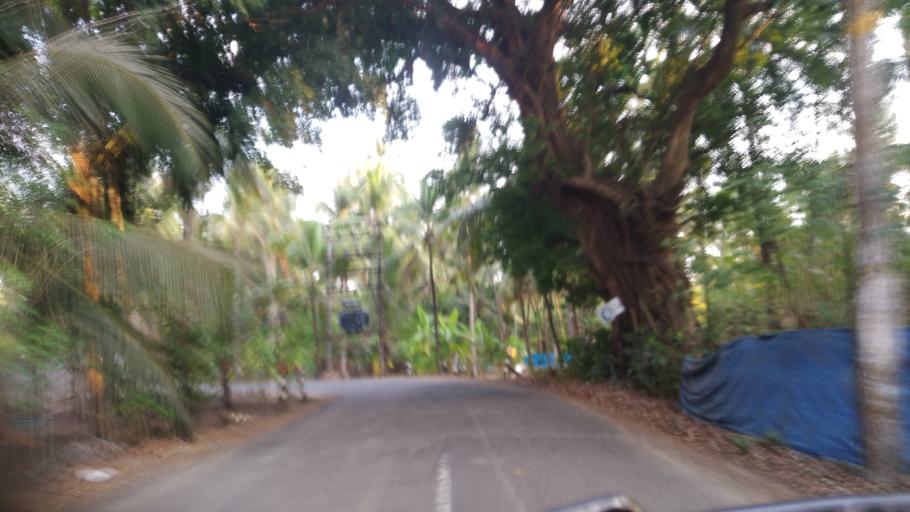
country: IN
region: Kerala
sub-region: Thrissur District
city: Thanniyam
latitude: 10.3778
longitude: 76.1020
